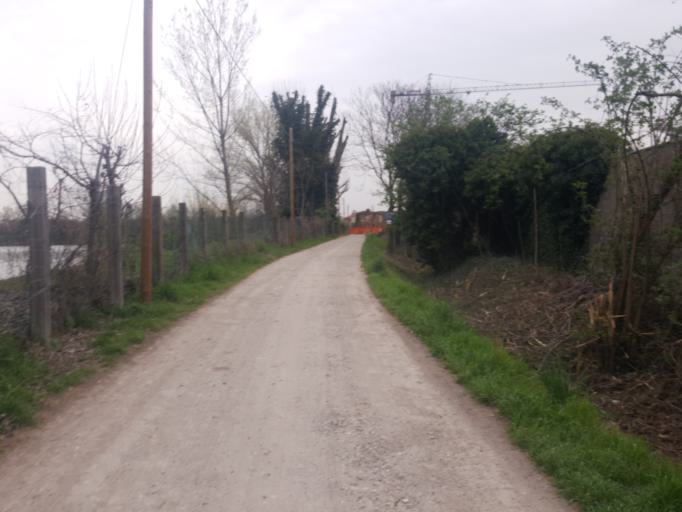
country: IT
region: Lombardy
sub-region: Citta metropolitana di Milano
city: Romano Banco
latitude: 45.4301
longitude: 9.1276
